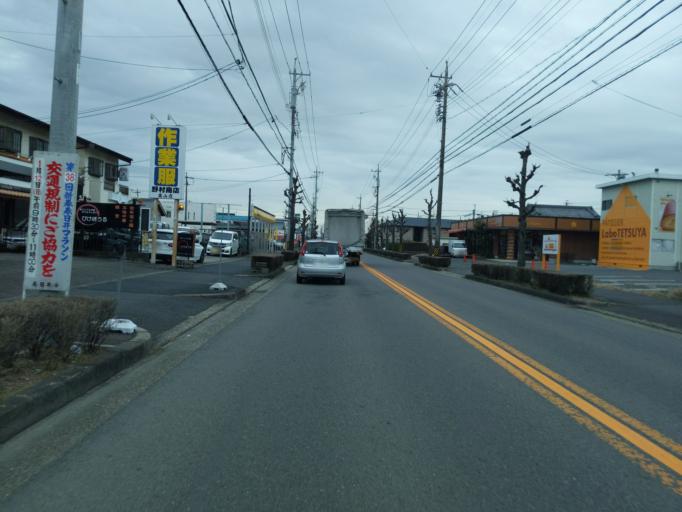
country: JP
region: Aichi
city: Kasugai
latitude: 35.2583
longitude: 136.9534
